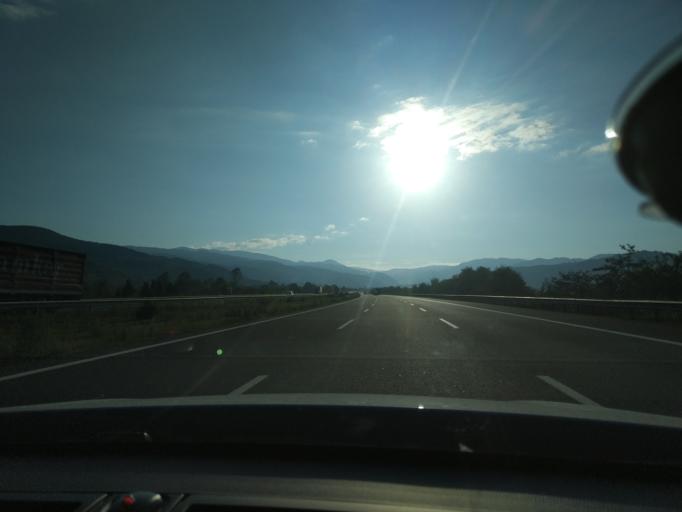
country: TR
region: Duzce
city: Kaynasli
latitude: 40.7844
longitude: 31.3020
